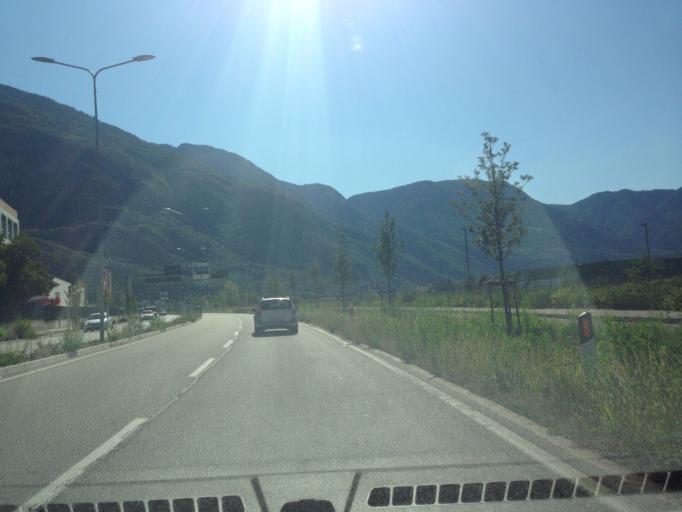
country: IT
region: Trentino-Alto Adige
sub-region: Bolzano
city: San Giacomo
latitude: 46.4701
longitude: 11.3183
